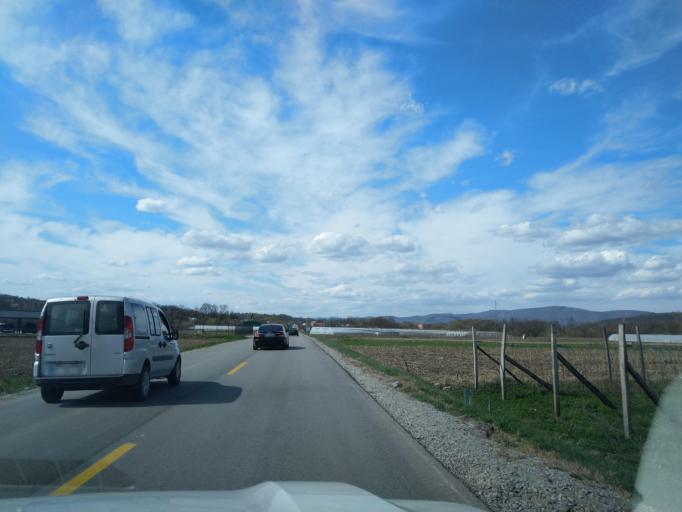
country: RS
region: Central Serbia
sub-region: Zlatiborski Okrug
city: Arilje
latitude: 43.7879
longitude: 20.1066
